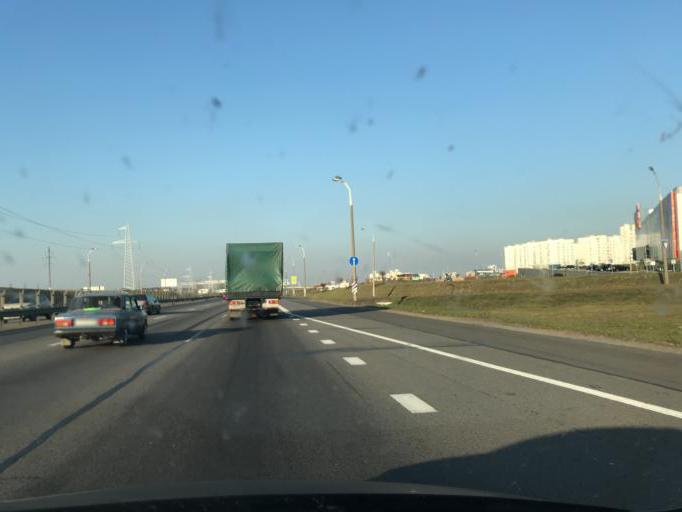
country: BY
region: Minsk
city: Zhdanovichy
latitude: 53.9118
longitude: 27.4104
